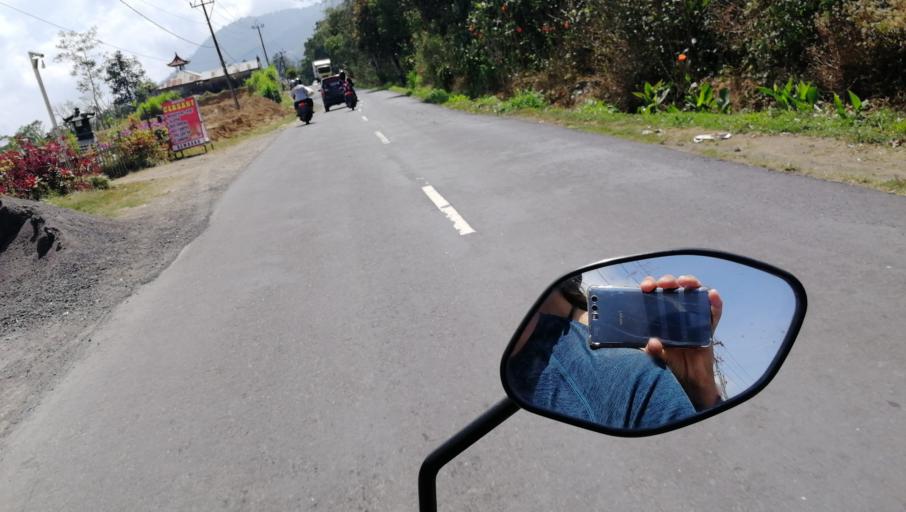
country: ID
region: Bali
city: Munduk
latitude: -8.2368
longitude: 115.1299
